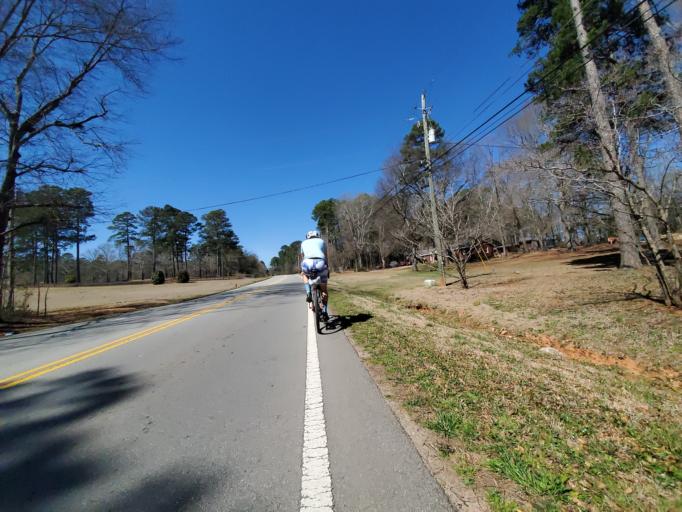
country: US
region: Georgia
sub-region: Barrow County
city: Russell
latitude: 33.9974
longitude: -83.6895
